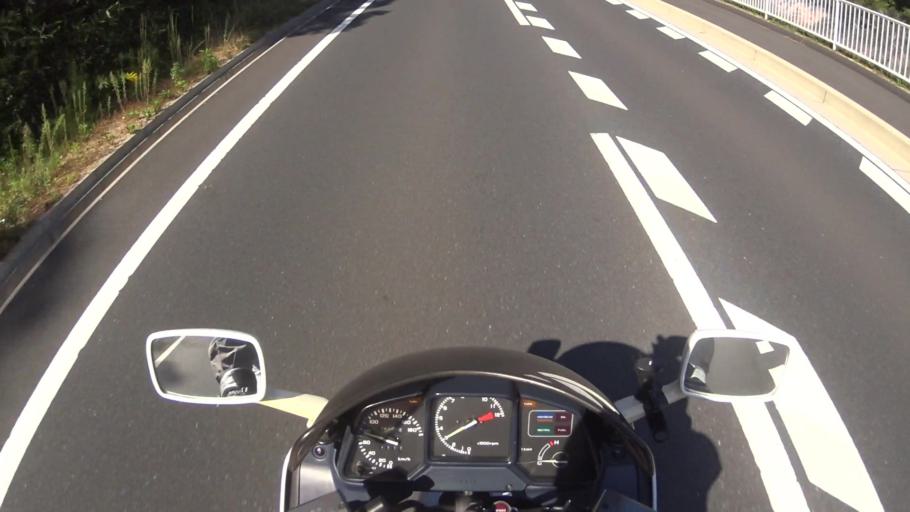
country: JP
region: Kyoto
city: Miyazu
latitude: 35.6725
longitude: 135.0754
